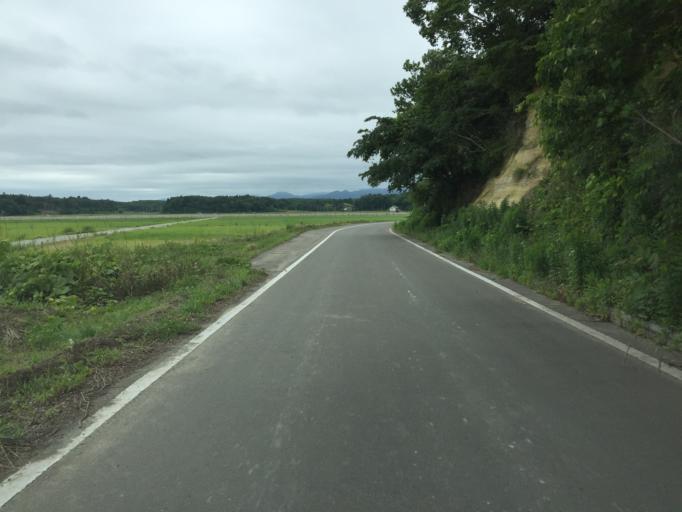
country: JP
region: Fukushima
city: Namie
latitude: 37.7393
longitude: 140.9817
